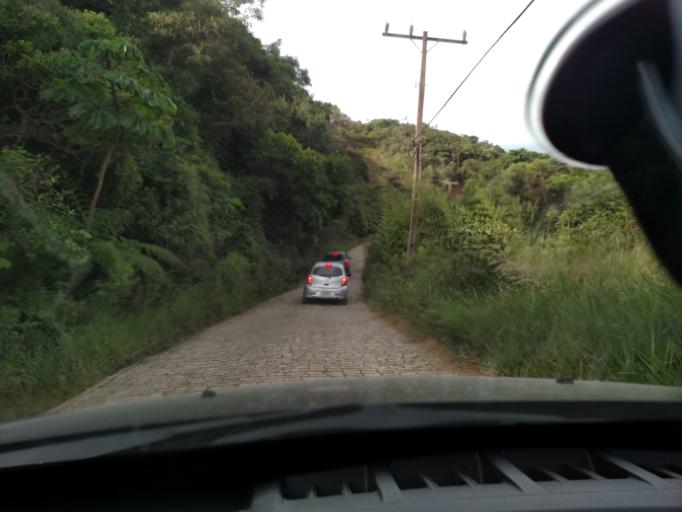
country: BR
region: Santa Catarina
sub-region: Porto Belo
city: Porto Belo
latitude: -27.2097
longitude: -48.4973
